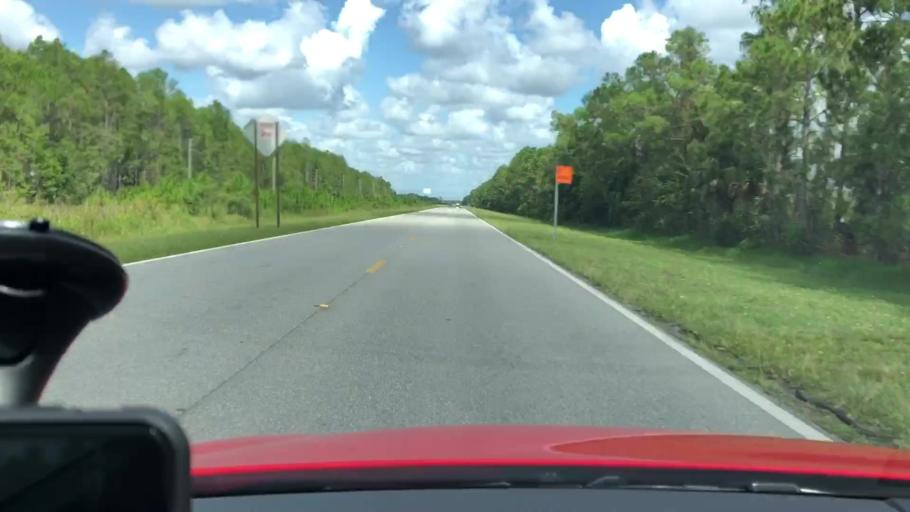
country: US
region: Florida
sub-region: Volusia County
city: Daytona Beach
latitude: 29.1829
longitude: -81.1197
